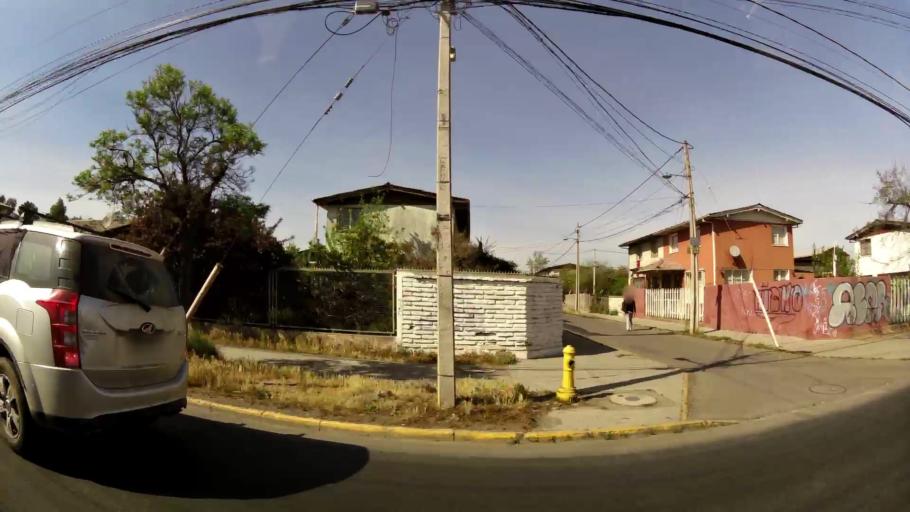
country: CL
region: Santiago Metropolitan
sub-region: Provincia de Cordillera
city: Puente Alto
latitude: -33.6033
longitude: -70.5795
